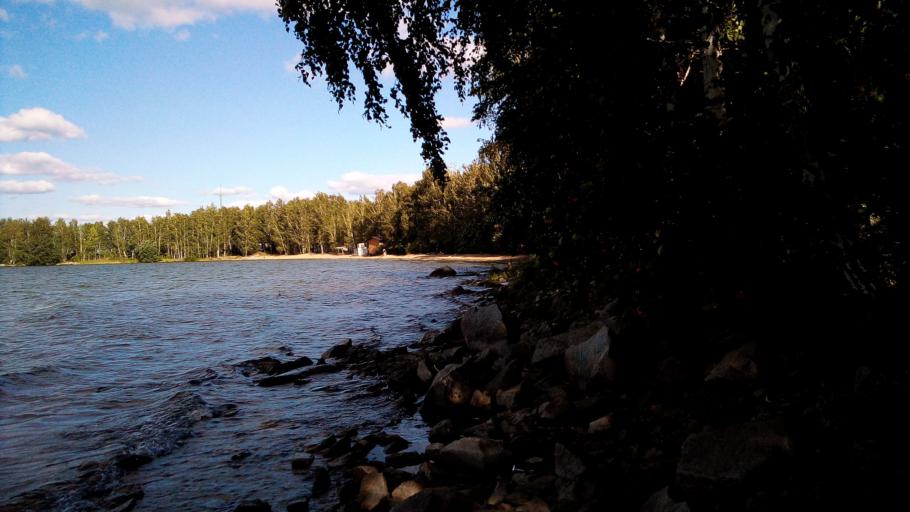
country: RU
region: Chelyabinsk
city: Tayginka
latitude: 55.4791
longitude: 60.4939
